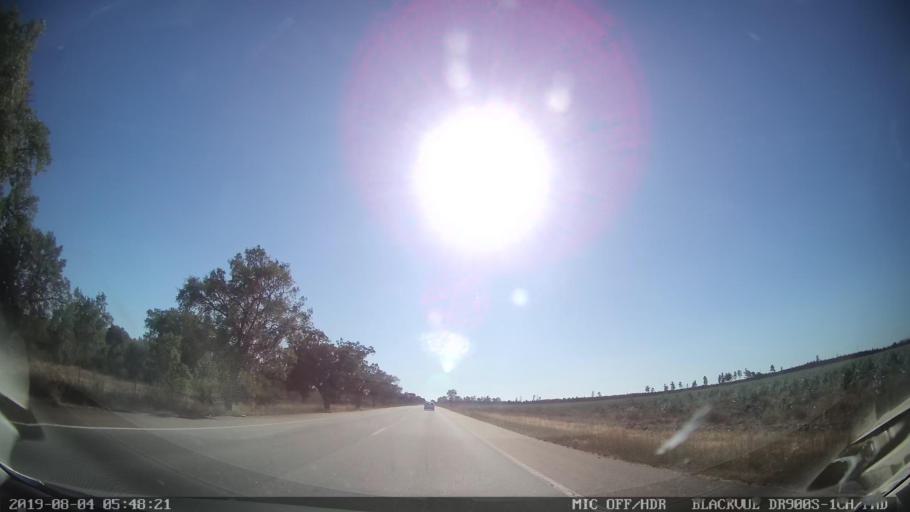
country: PT
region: Portalegre
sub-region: Gaviao
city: Gaviao
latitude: 39.4449
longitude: -7.8236
